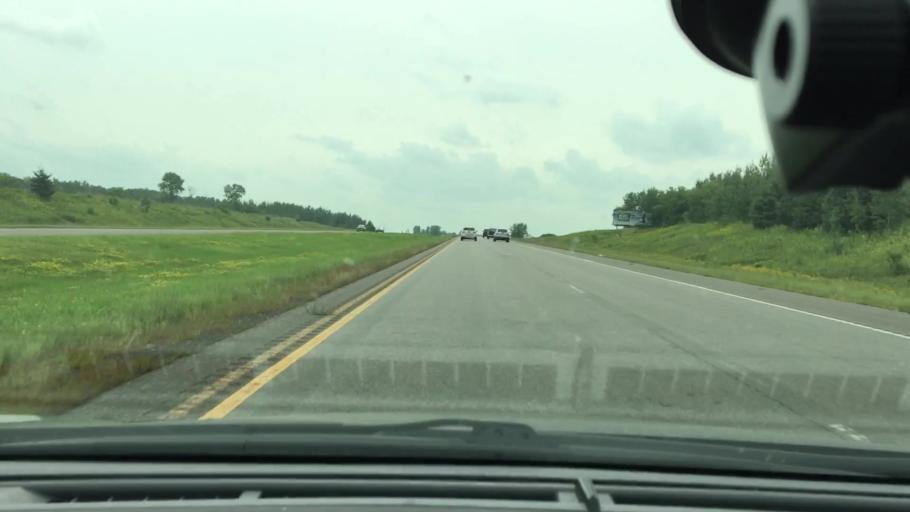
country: US
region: Minnesota
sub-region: Mille Lacs County
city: Milaca
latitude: 45.7739
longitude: -93.6468
